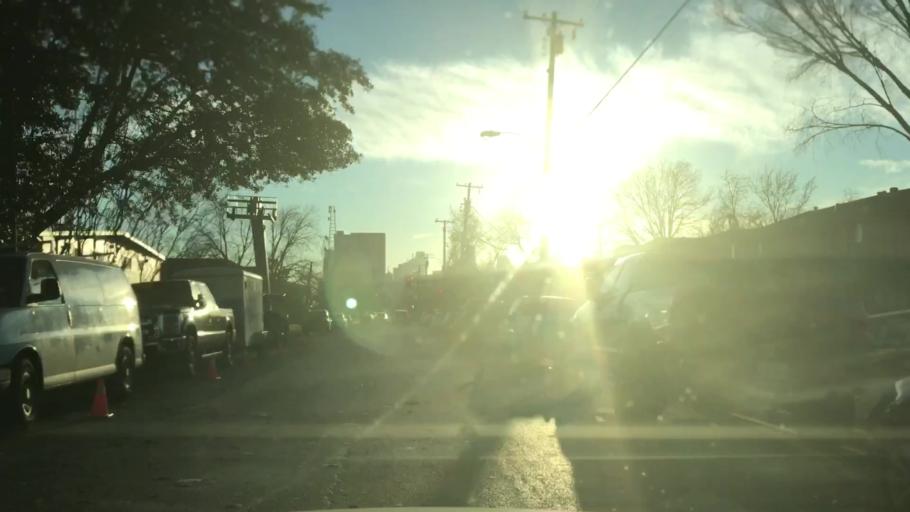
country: US
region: Texas
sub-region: Dallas County
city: Highland Park
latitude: 32.8055
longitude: -96.7716
